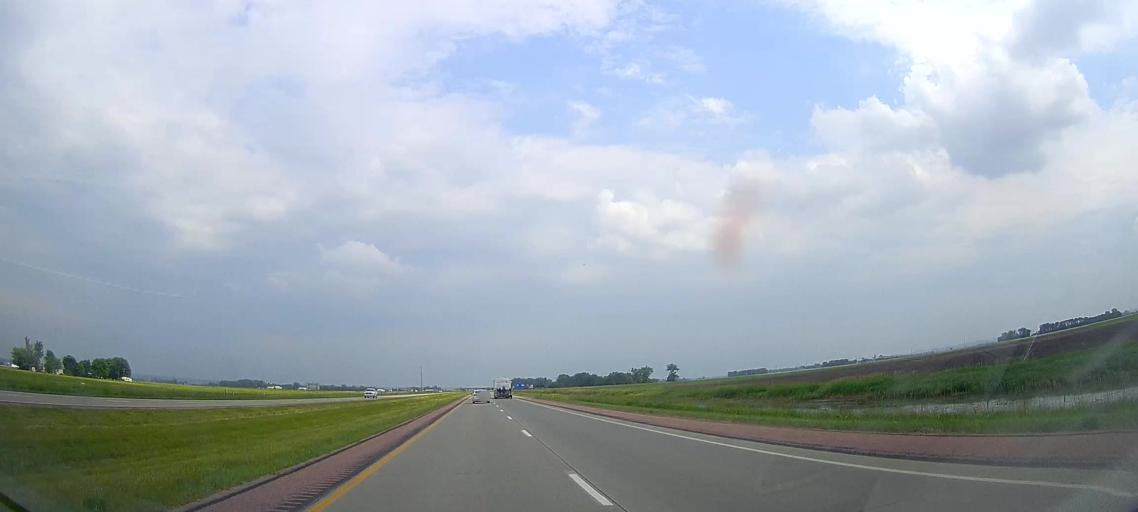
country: US
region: South Dakota
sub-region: Union County
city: Elk Point
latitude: 42.6172
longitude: -96.5916
